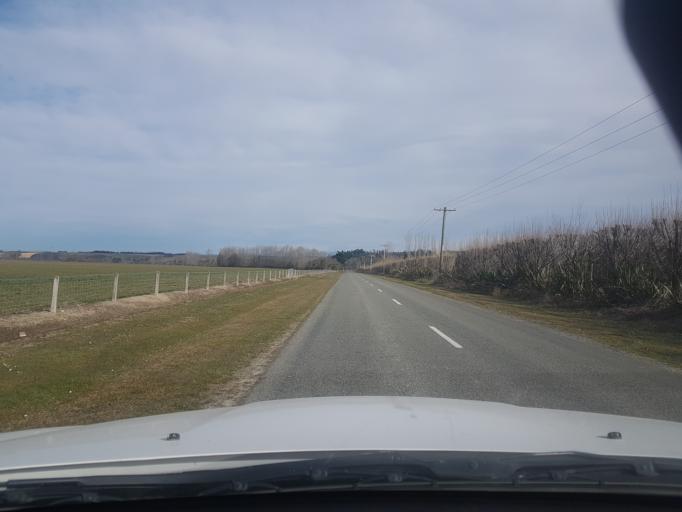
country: NZ
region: Canterbury
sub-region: Timaru District
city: Pleasant Point
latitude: -44.1240
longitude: 171.1929
